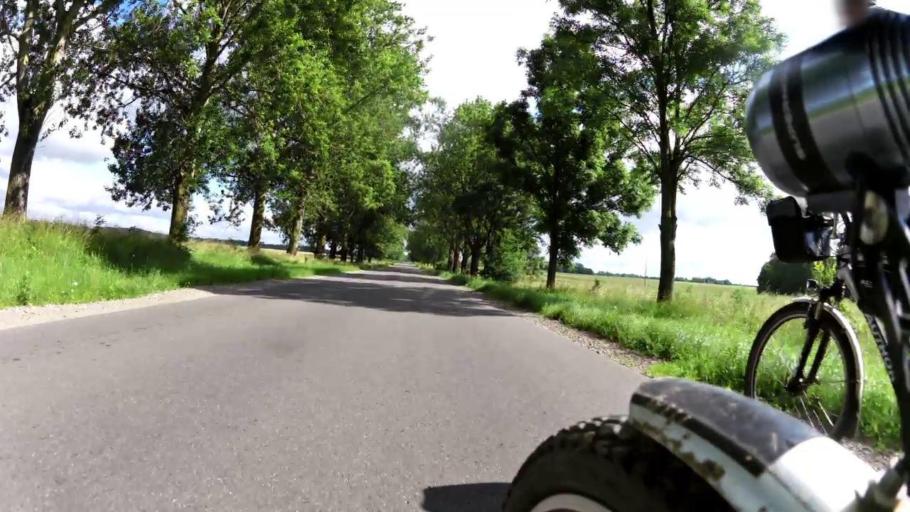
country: PL
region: West Pomeranian Voivodeship
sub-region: Powiat swidwinski
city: Rabino
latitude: 53.7871
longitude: 15.9025
